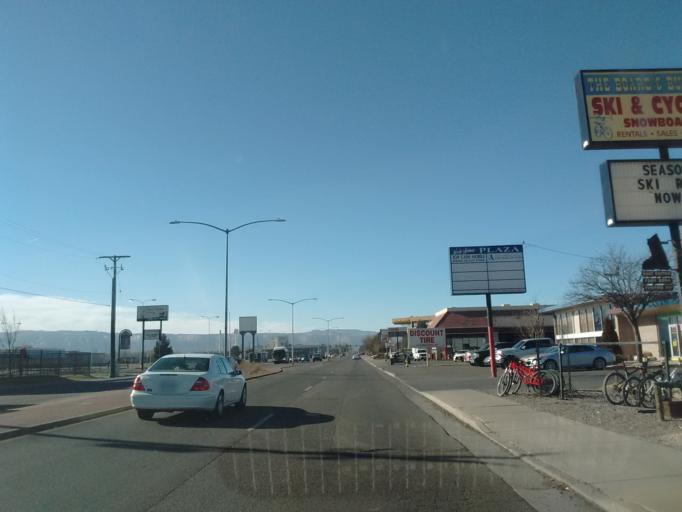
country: US
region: Colorado
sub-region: Mesa County
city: Grand Junction
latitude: 39.0774
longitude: -108.5298
